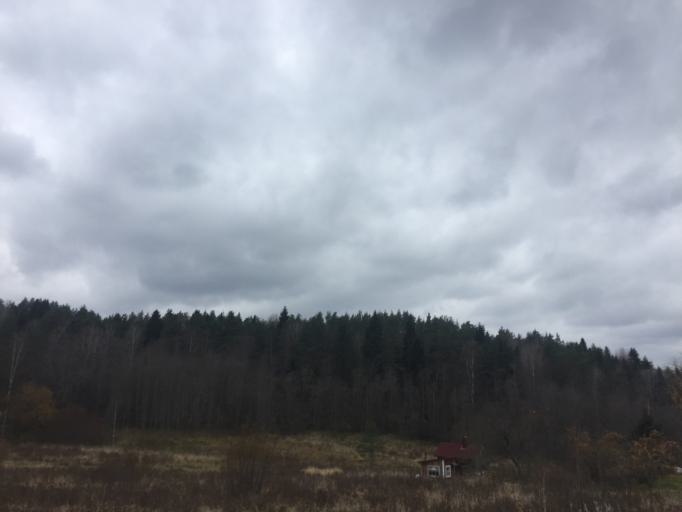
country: RU
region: Republic of Karelia
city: Lakhdenpokh'ya
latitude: 61.4350
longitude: 30.1482
